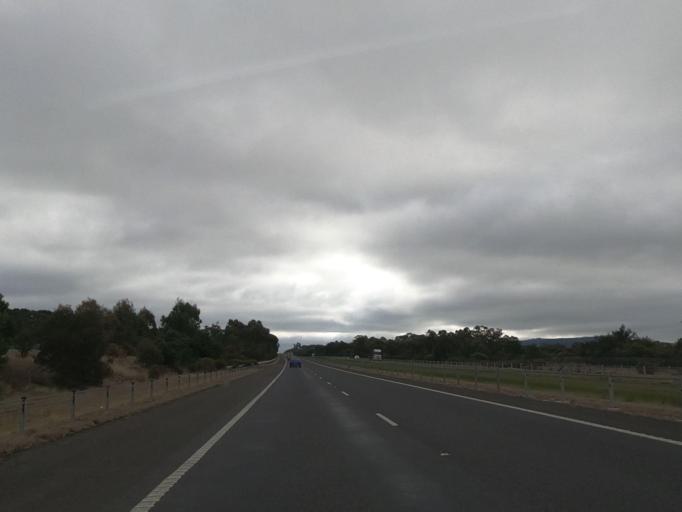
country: AU
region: Victoria
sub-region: Mount Alexander
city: Castlemaine
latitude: -37.0728
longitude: 144.3131
